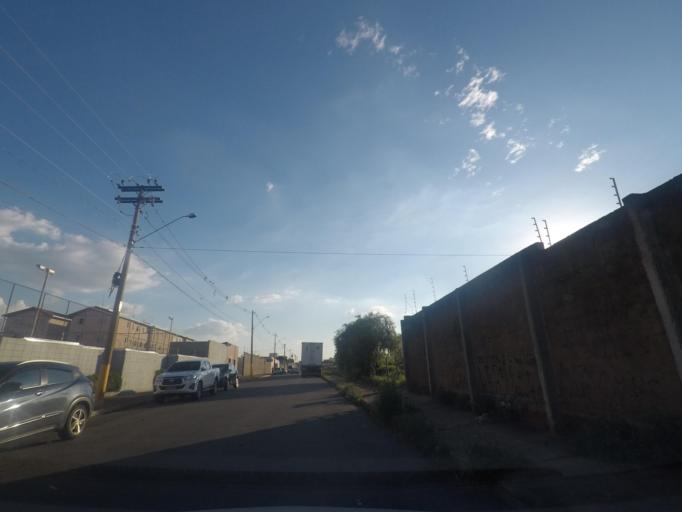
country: BR
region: Sao Paulo
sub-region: Sumare
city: Sumare
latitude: -22.8177
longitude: -47.2854
